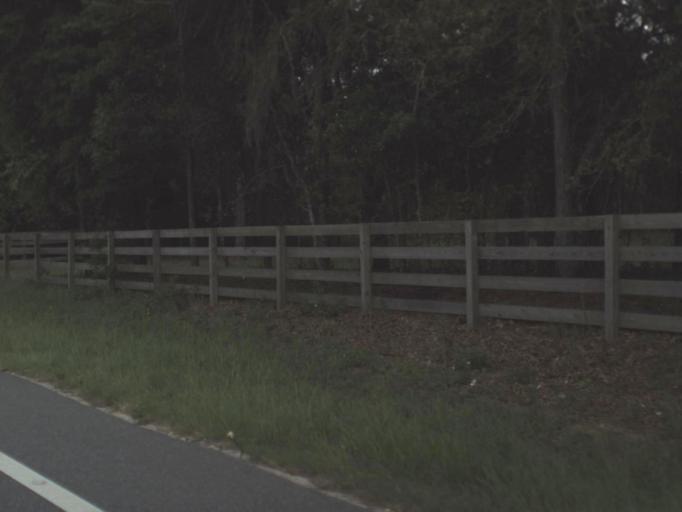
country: US
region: Florida
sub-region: Clay County
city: Keystone Heights
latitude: 29.7449
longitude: -81.9802
